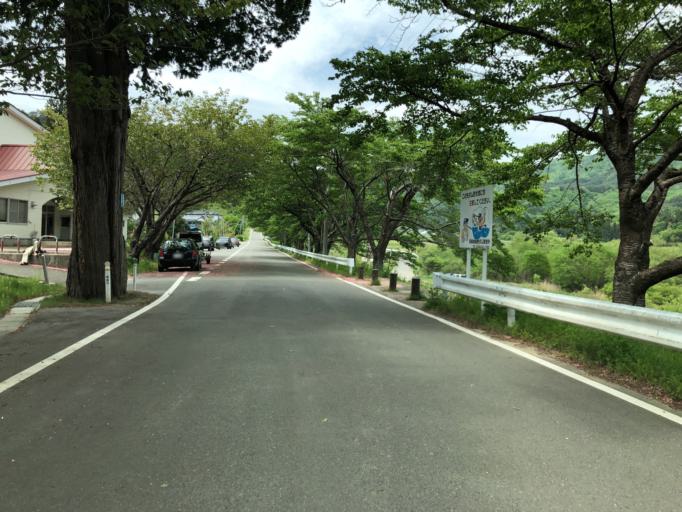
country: JP
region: Miyagi
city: Marumori
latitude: 37.7321
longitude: 140.8083
